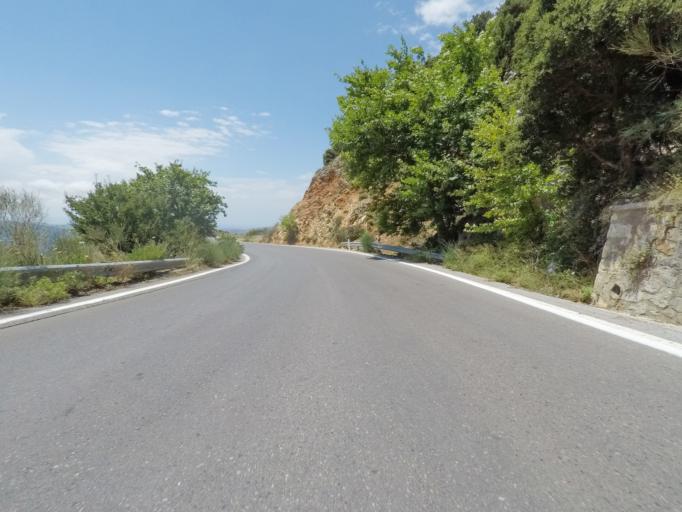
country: GR
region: Crete
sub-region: Nomos Irakleiou
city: Mokhos
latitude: 35.2137
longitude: 25.4620
